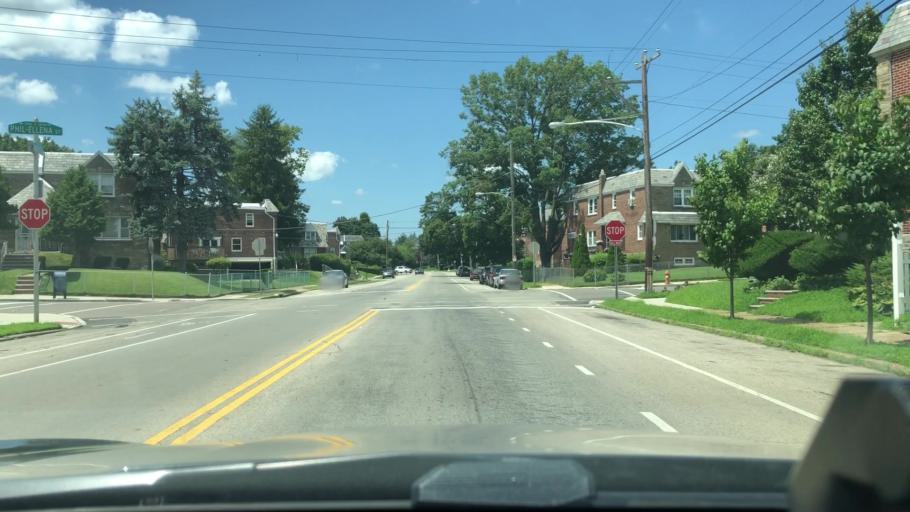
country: US
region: Pennsylvania
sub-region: Montgomery County
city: Wyndmoor
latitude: 40.0649
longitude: -75.1712
